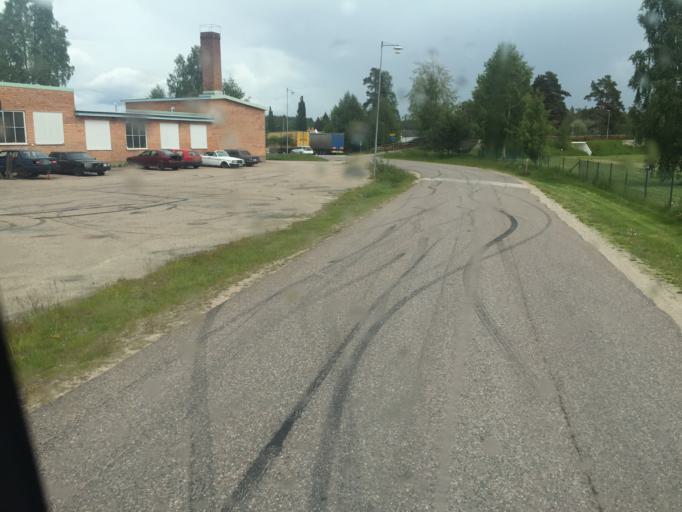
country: SE
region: Dalarna
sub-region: Vansbro Kommun
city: Vansbro
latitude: 60.5076
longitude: 14.2296
